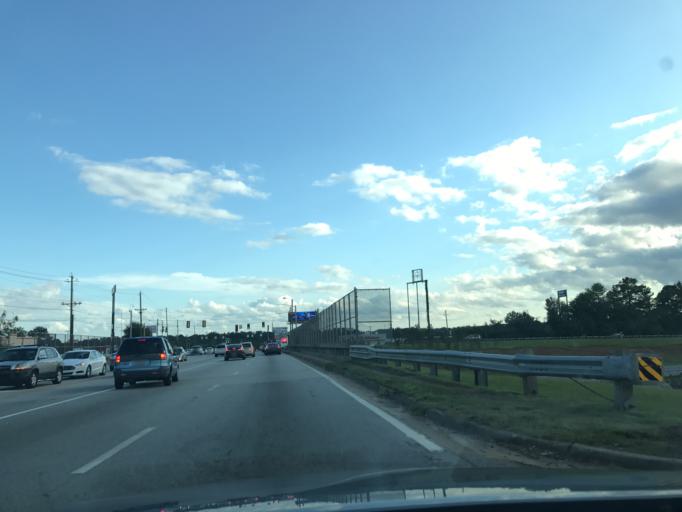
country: US
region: Georgia
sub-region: Douglas County
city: Douglasville
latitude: 33.7287
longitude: -84.7622
